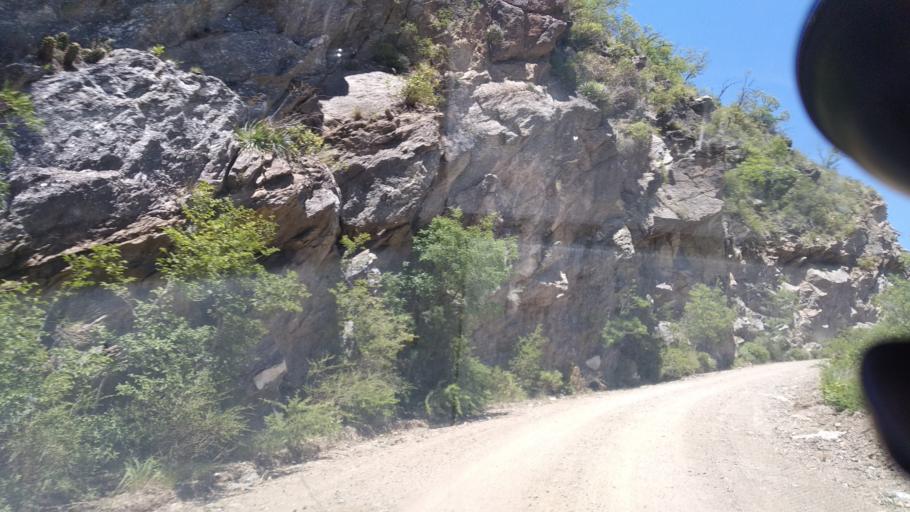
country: AR
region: Cordoba
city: Salsacate
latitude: -31.3739
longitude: -65.4069
